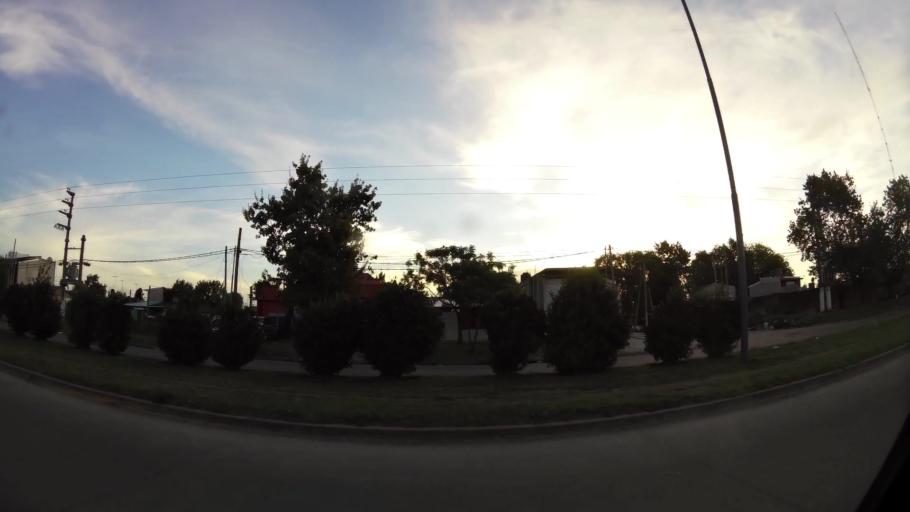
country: AR
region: Buenos Aires
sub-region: Partido de Quilmes
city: Quilmes
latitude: -34.7840
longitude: -58.2223
